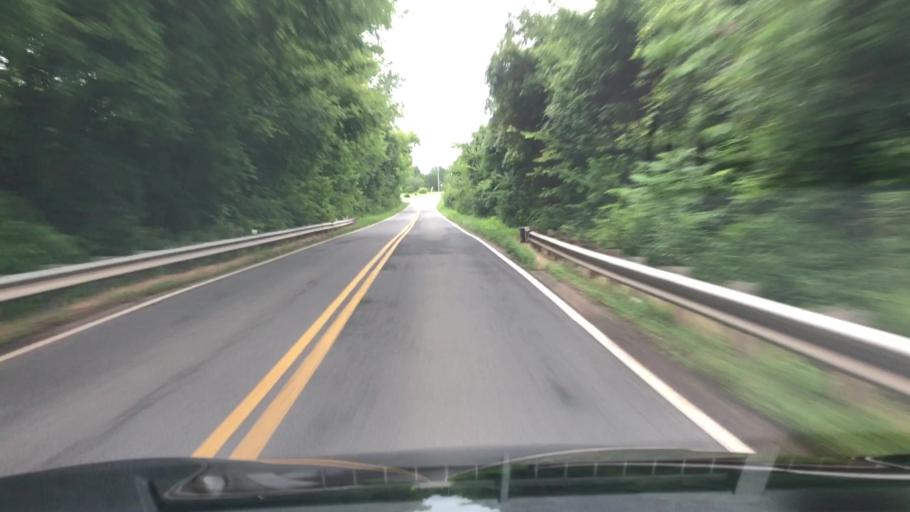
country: US
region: Virginia
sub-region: Prince William County
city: Nokesville
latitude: 38.6063
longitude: -77.6052
